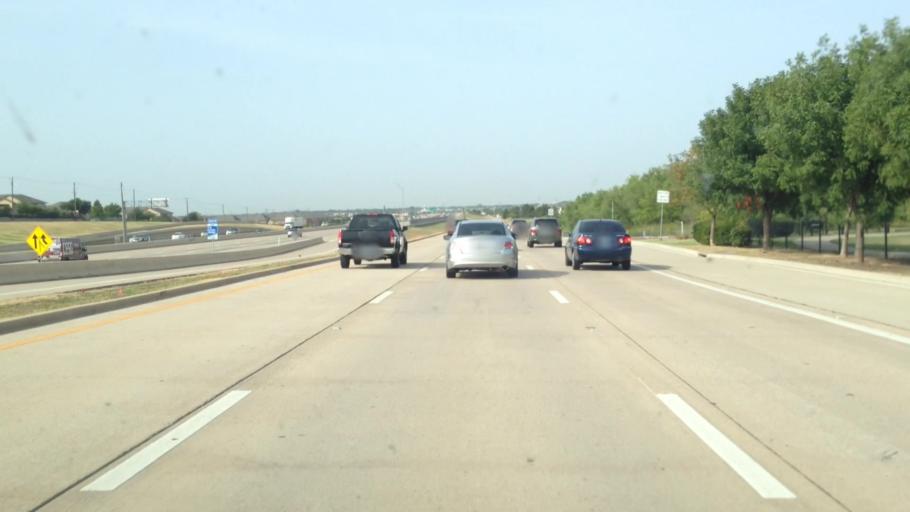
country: US
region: Texas
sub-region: Denton County
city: Lewisville
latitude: 33.0334
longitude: -96.9270
